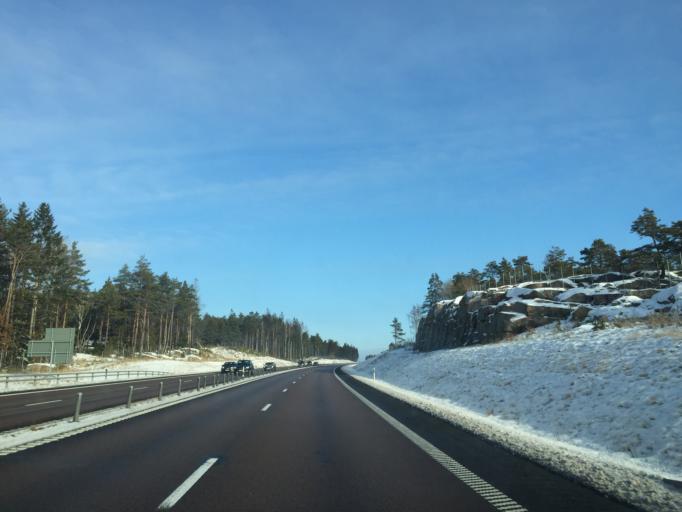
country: SE
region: Vaestra Goetaland
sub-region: Tanums Kommun
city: Tanumshede
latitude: 58.7786
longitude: 11.2739
